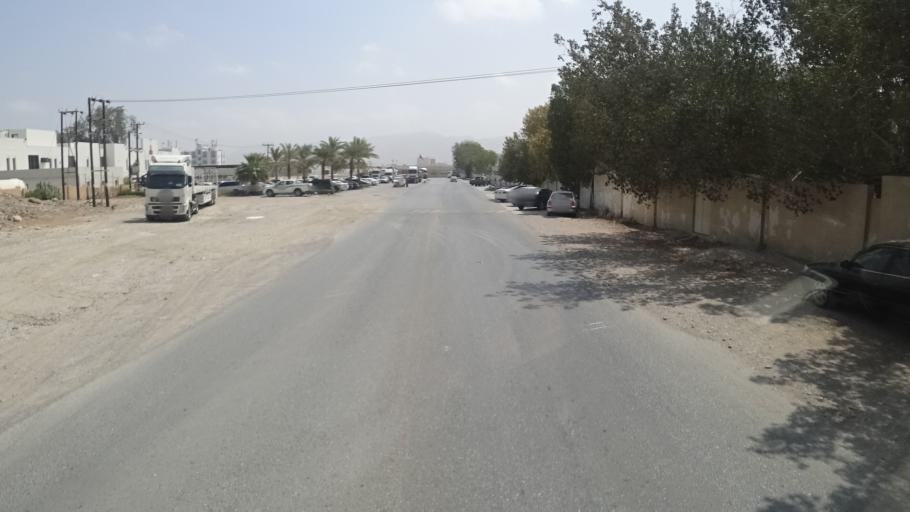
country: OM
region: Muhafazat Masqat
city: Bawshar
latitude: 23.5750
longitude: 58.3572
